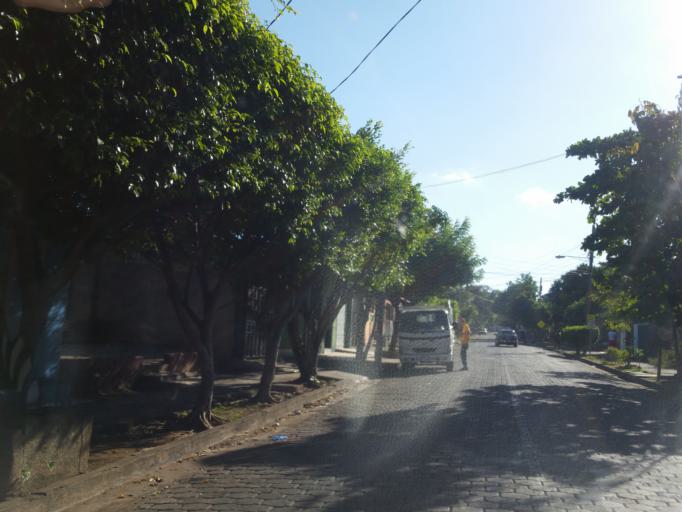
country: NI
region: Managua
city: Managua
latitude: 12.1351
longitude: -86.2898
